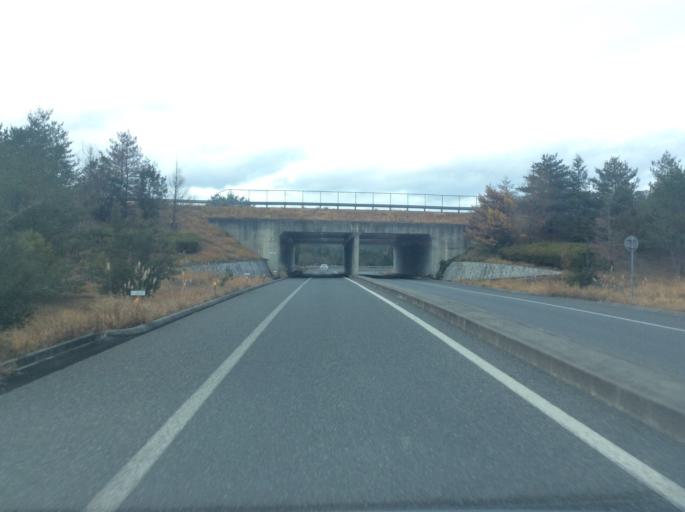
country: JP
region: Fukushima
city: Iwaki
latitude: 37.1264
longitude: 140.9459
